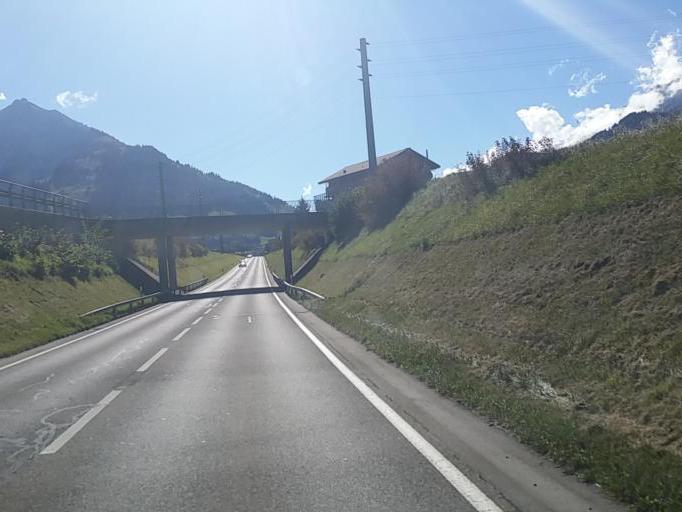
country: CH
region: Bern
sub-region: Frutigen-Niedersimmental District
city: Frutigen
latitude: 46.5921
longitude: 7.6565
